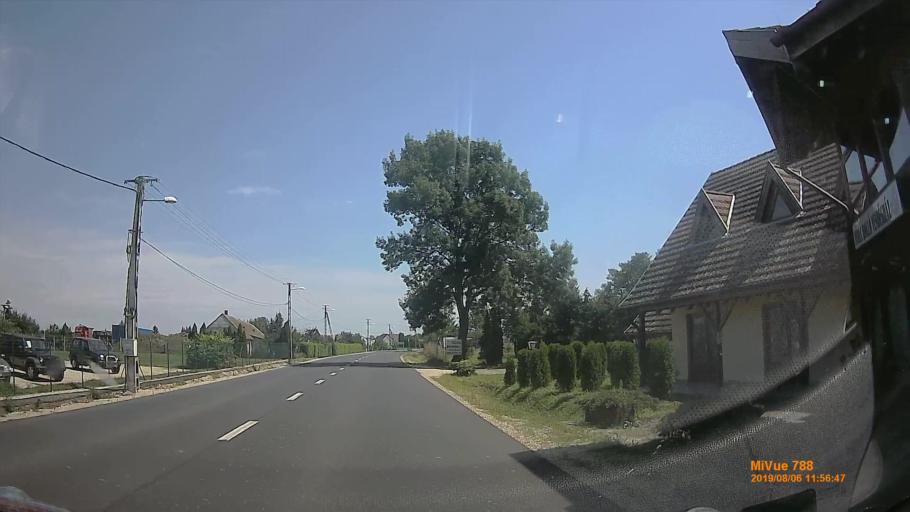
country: HU
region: Vas
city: Vasvar
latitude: 47.0576
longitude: 16.7004
